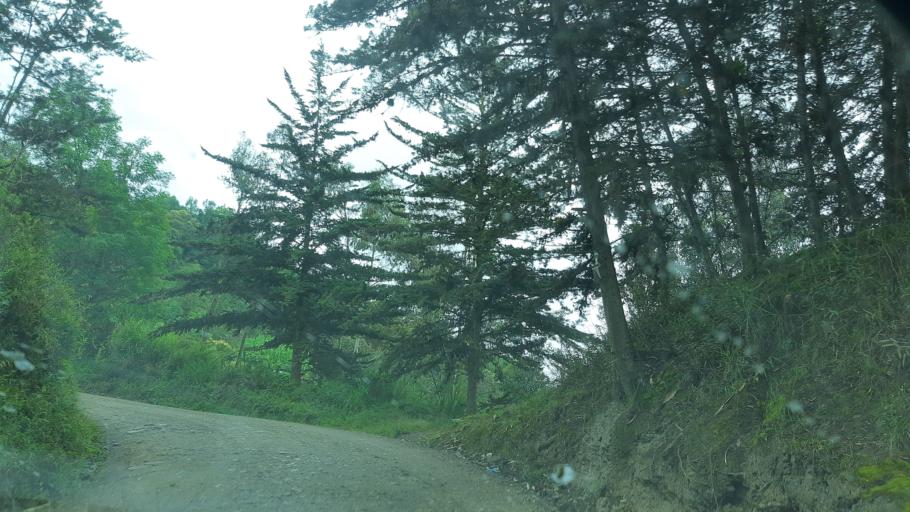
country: CO
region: Boyaca
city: Guateque
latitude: 5.0319
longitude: -73.4467
